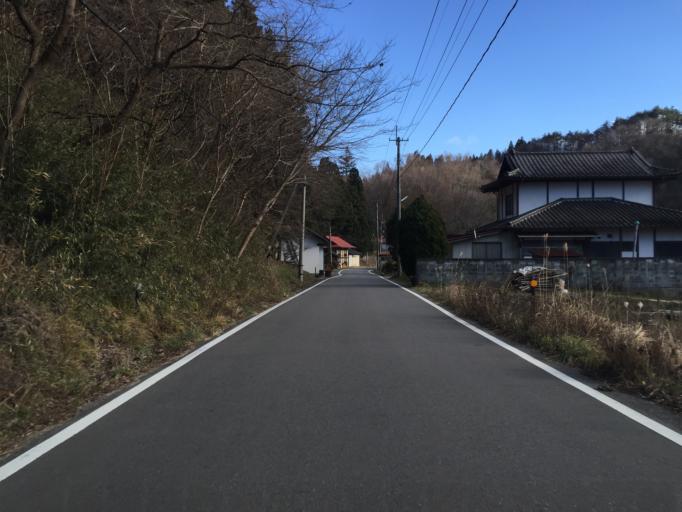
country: JP
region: Fukushima
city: Funehikimachi-funehiki
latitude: 37.2404
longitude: 140.6859
